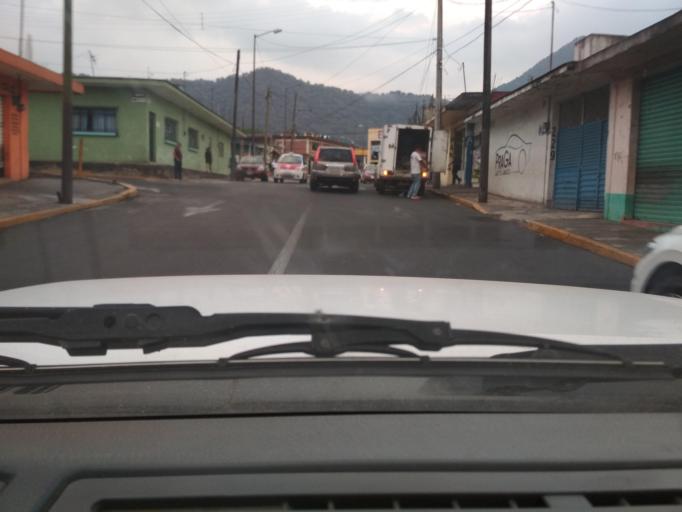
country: MX
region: Veracruz
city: Orizaba
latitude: 18.8665
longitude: -97.1012
